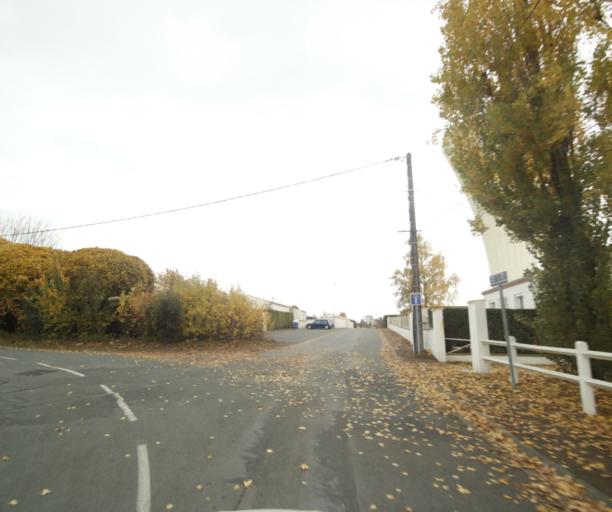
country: FR
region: Poitou-Charentes
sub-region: Departement de la Charente-Maritime
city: Saintes
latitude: 45.7322
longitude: -0.6531
